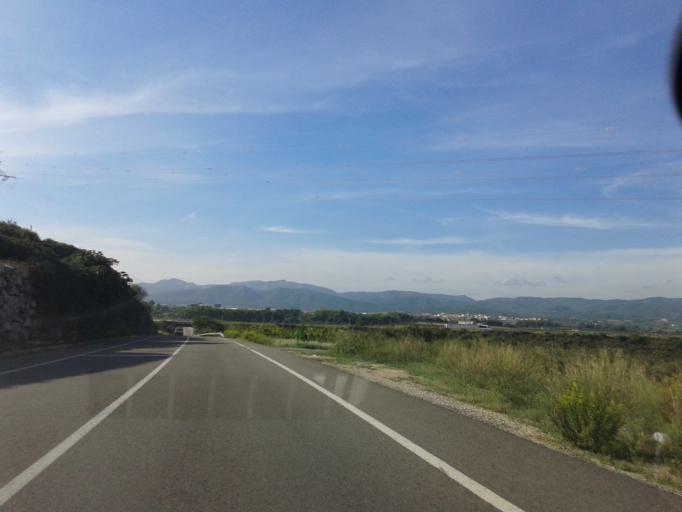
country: ES
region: Catalonia
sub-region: Provincia de Tarragona
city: Sant Jaume dels Domenys
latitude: 41.2819
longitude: 1.5795
